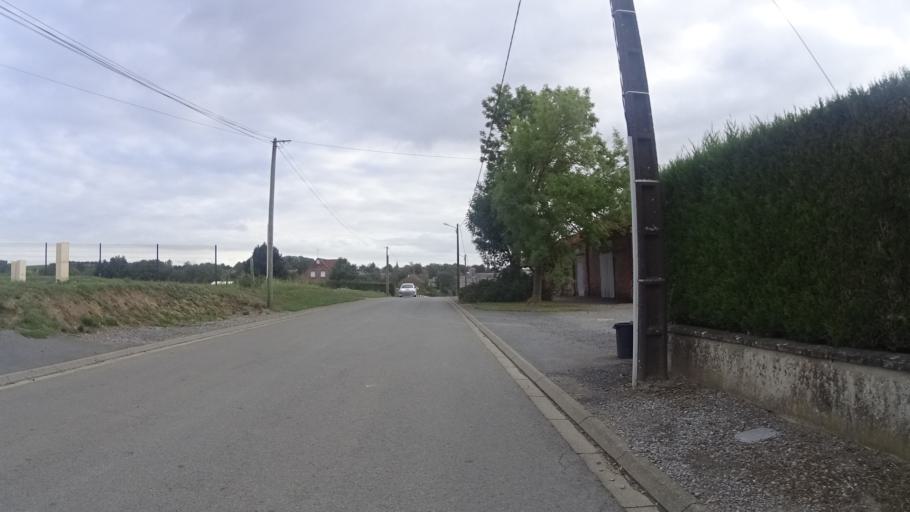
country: FR
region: Picardie
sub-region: Departement de l'Aisne
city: Guise
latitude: 49.9314
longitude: 3.5801
